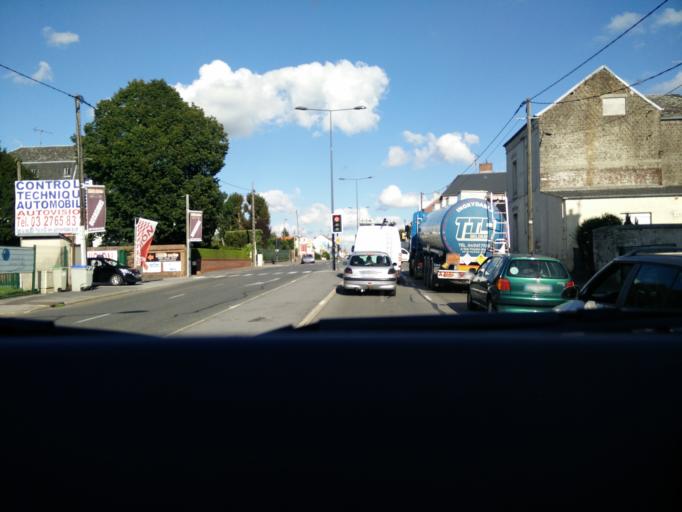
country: FR
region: Nord-Pas-de-Calais
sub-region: Departement du Nord
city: Maubeuge
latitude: 50.2821
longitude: 3.9609
